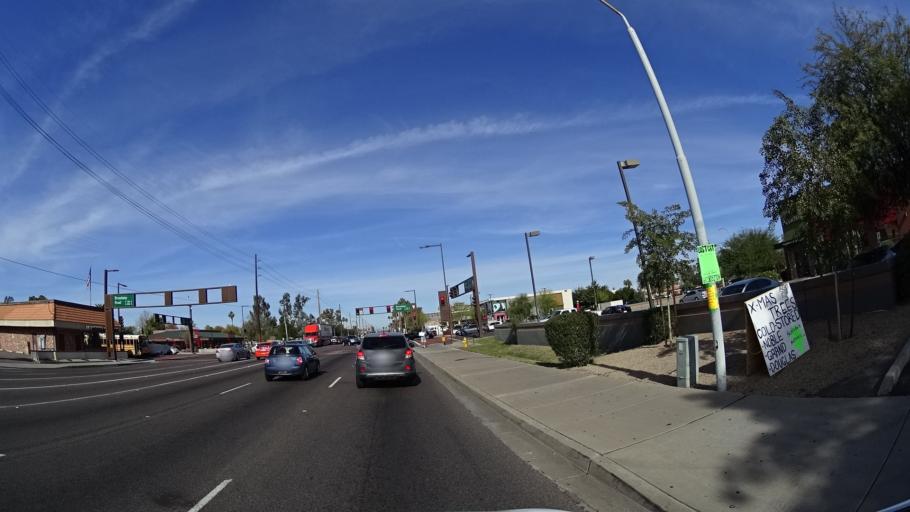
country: US
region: Arizona
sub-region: Maricopa County
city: Tempe
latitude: 33.4069
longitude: -111.9262
